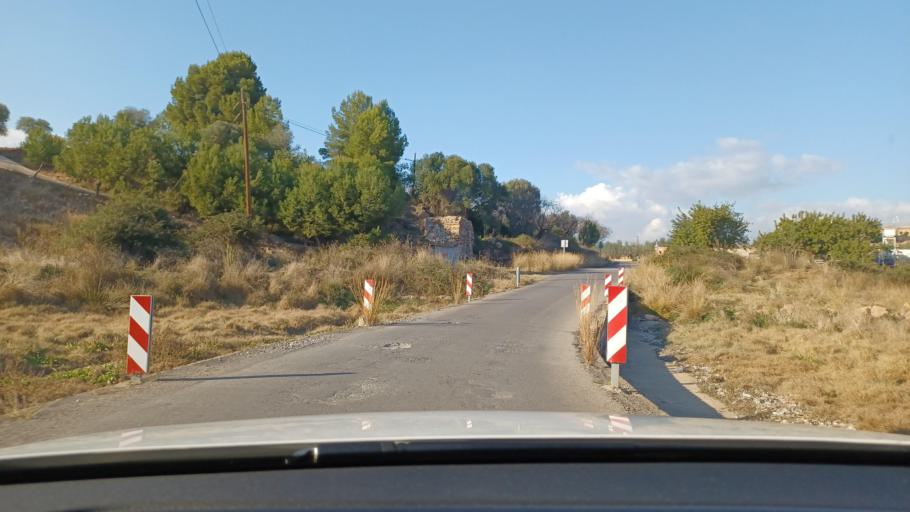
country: ES
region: Valencia
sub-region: Provincia de Castello
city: Onda
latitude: 39.9577
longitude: -0.2498
